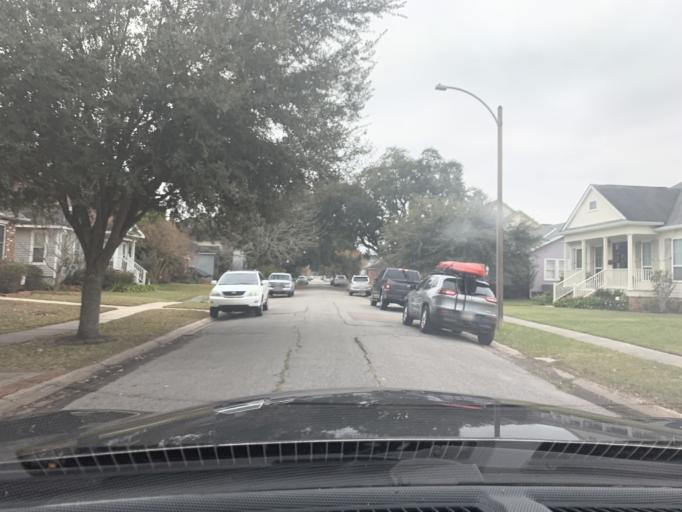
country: US
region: Louisiana
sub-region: Jefferson Parish
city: Metairie
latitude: 30.0121
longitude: -90.1105
